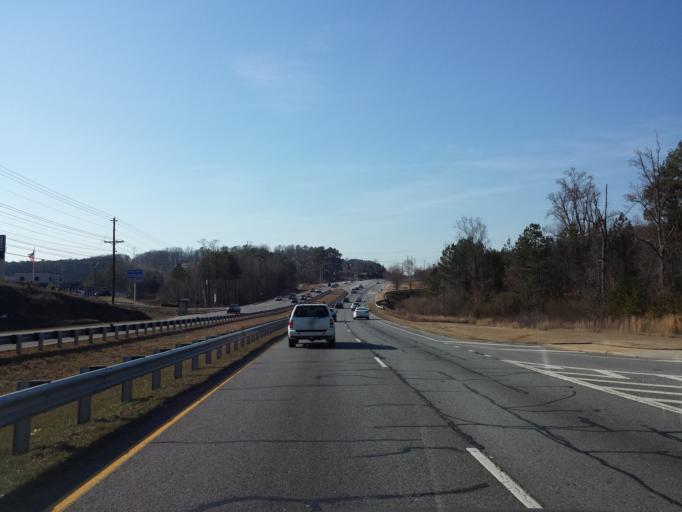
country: US
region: Georgia
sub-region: Cobb County
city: Marietta
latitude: 33.9879
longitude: -84.5731
